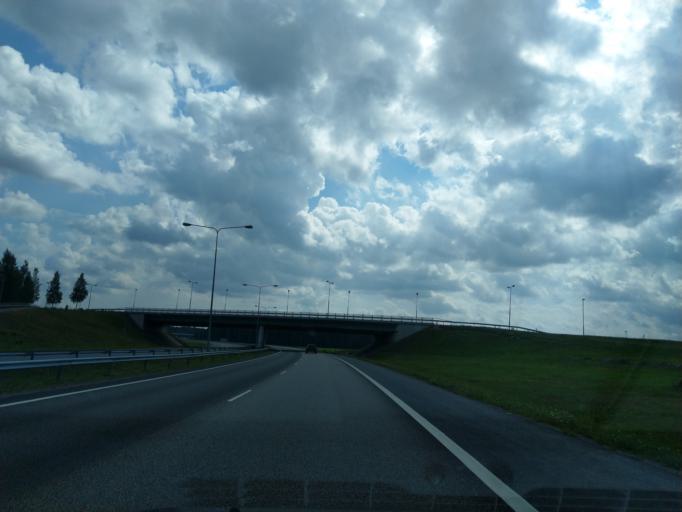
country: FI
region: South Karelia
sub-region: Imatra
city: Ruokolahti
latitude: 61.2229
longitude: 28.8477
